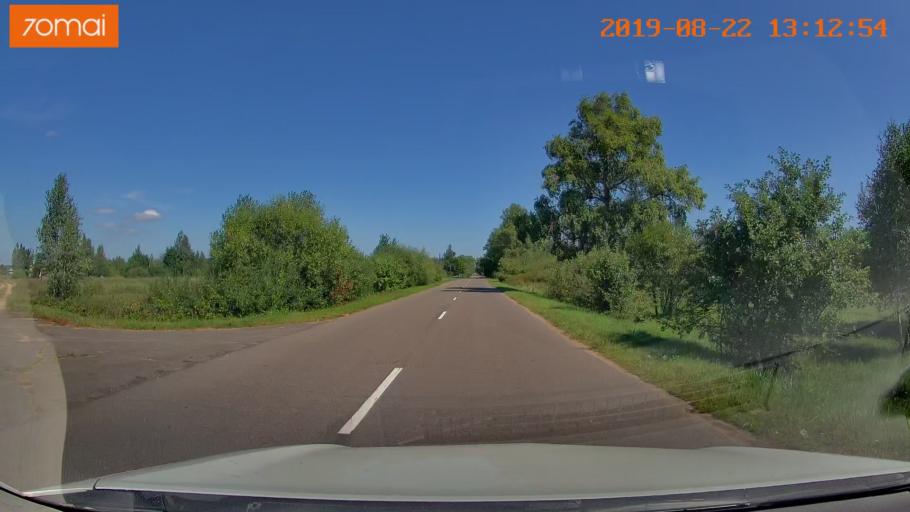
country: BY
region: Minsk
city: Prawdzinski
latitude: 53.2683
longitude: 27.8691
